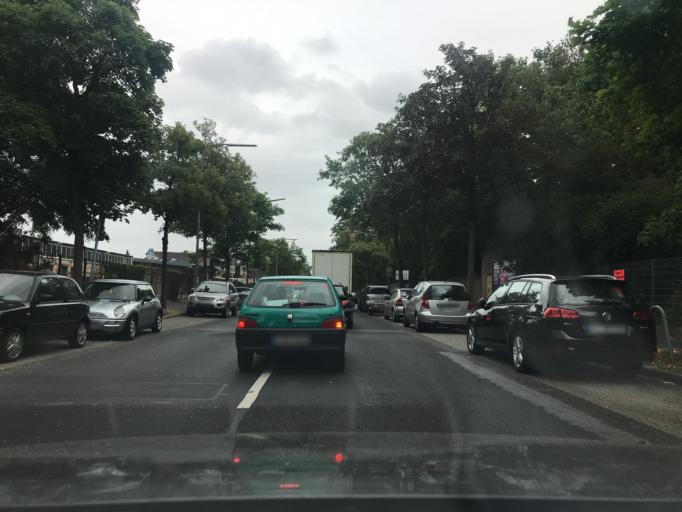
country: DE
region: North Rhine-Westphalia
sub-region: Regierungsbezirk Dusseldorf
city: Erkrath
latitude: 51.1816
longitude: 6.8572
